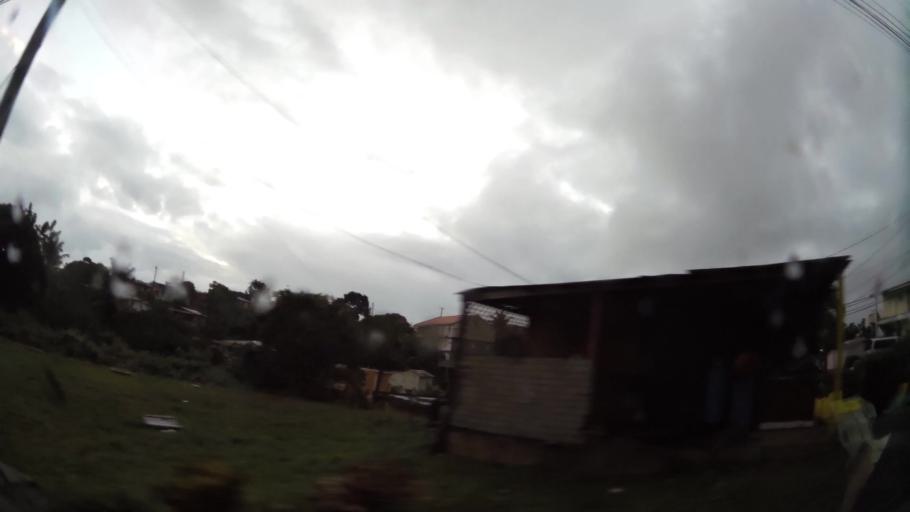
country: DM
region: Saint Andrew
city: Wesley
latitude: 15.5642
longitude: -61.3109
